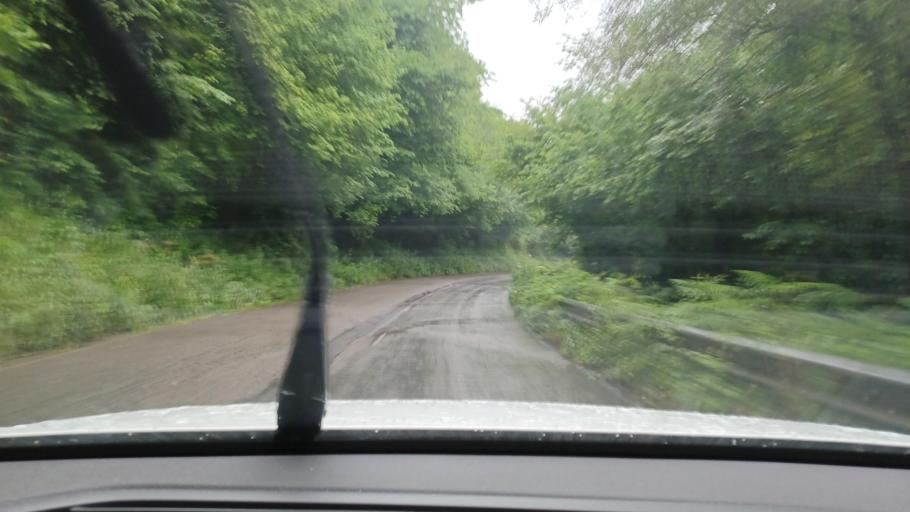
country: ES
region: Asturias
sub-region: Province of Asturias
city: Castandiello
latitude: 43.3087
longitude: -5.9003
